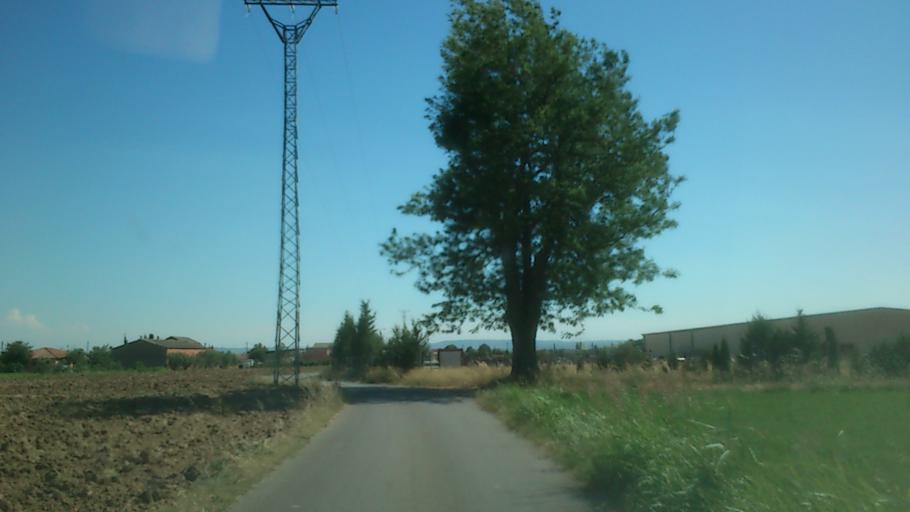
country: ES
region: Aragon
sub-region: Provincia de Zaragoza
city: Villanueva de Gallego
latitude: 41.7021
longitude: -0.8116
